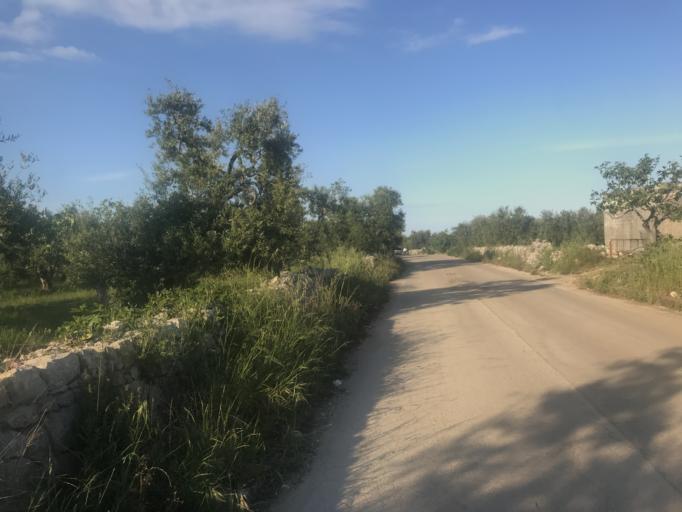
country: IT
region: Apulia
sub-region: Provincia di Bari
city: Corato
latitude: 41.1607
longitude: 16.4189
